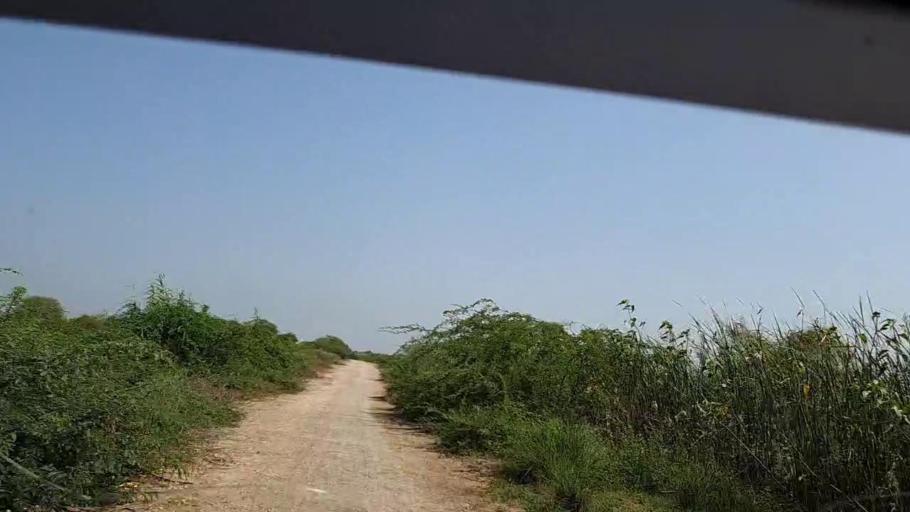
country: PK
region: Sindh
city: Rajo Khanani
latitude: 24.9376
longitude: 68.8728
